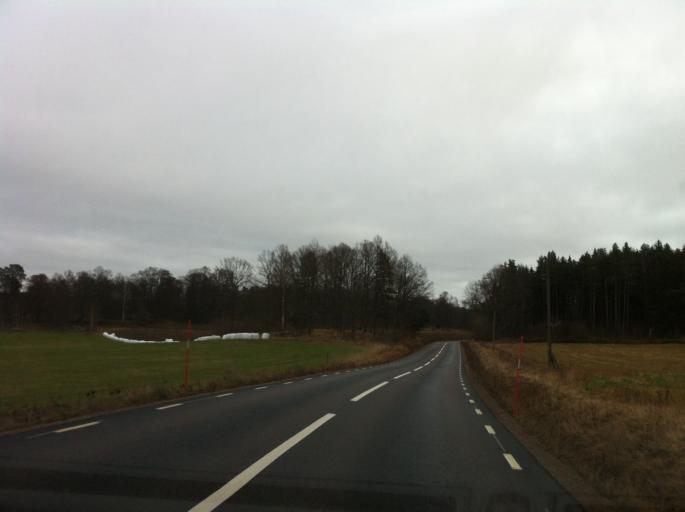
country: SE
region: Kalmar
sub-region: Vasterviks Kommun
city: Overum
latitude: 57.9064
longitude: 16.2059
